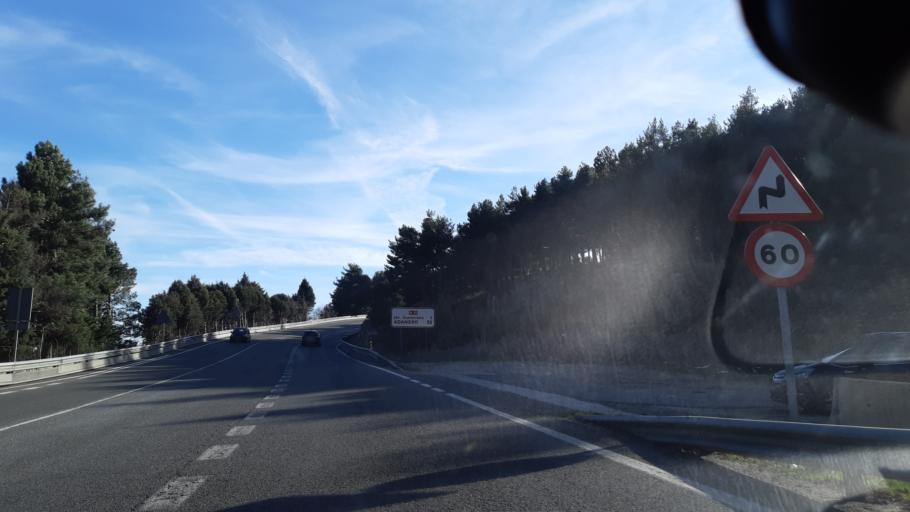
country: ES
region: Madrid
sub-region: Provincia de Madrid
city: Guadarrama
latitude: 40.7090
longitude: -4.1288
